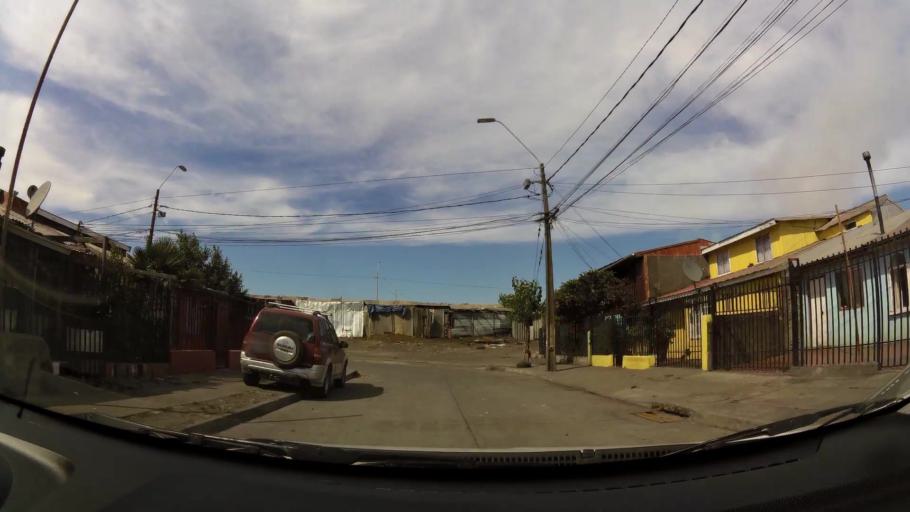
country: CL
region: Biobio
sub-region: Provincia de Concepcion
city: Talcahuano
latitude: -36.7360
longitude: -73.1179
